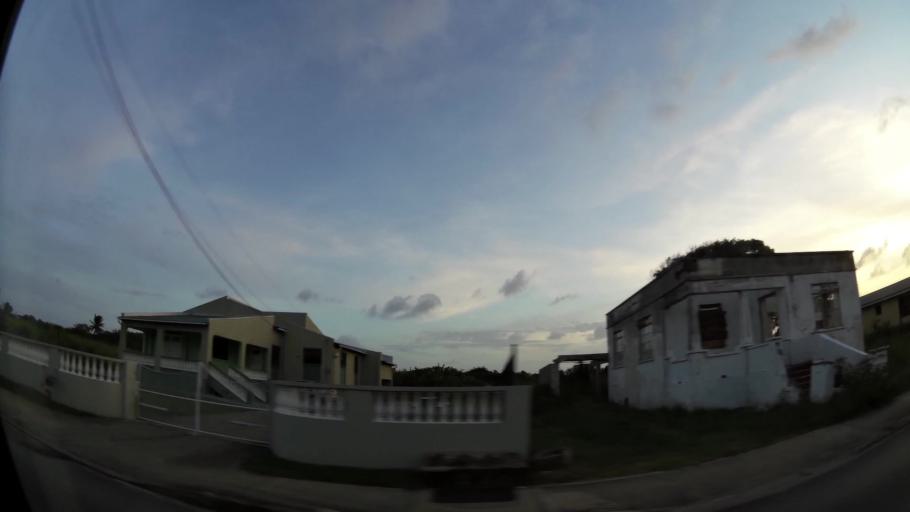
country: BB
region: Saint Philip
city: Crane
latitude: 13.1049
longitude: -59.4634
